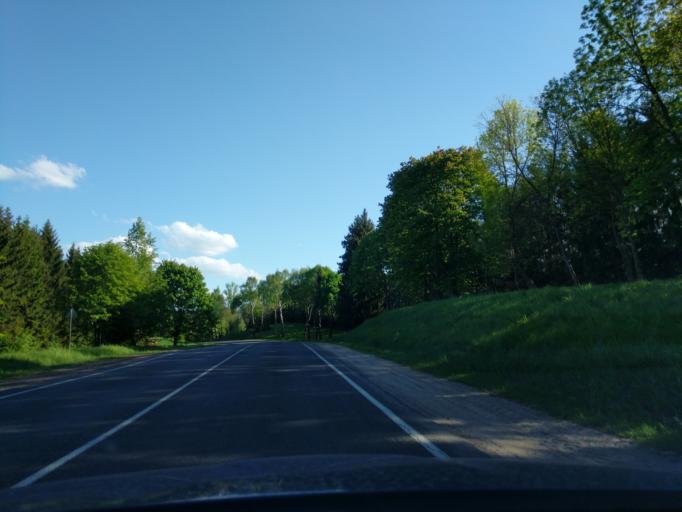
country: BY
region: Minsk
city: Myadzyel
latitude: 54.8556
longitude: 26.9237
